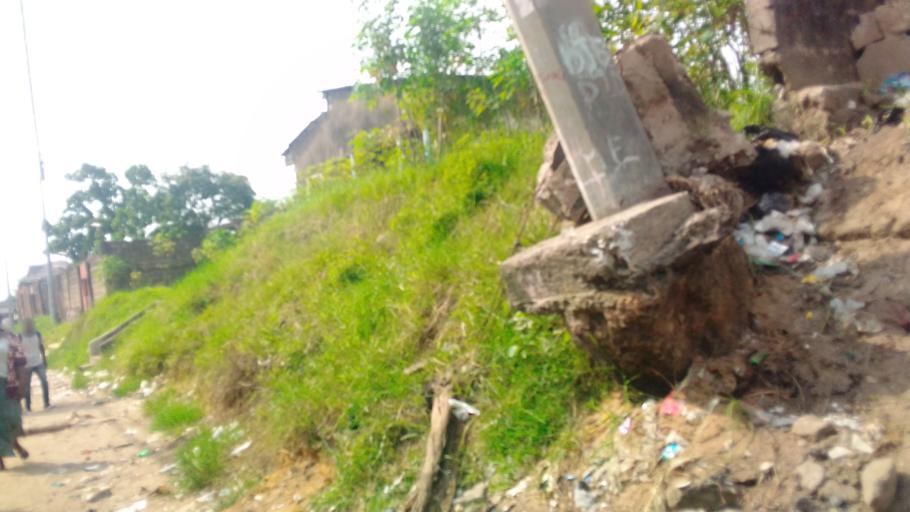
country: CD
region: Kinshasa
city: Masina
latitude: -4.3978
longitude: 15.3439
